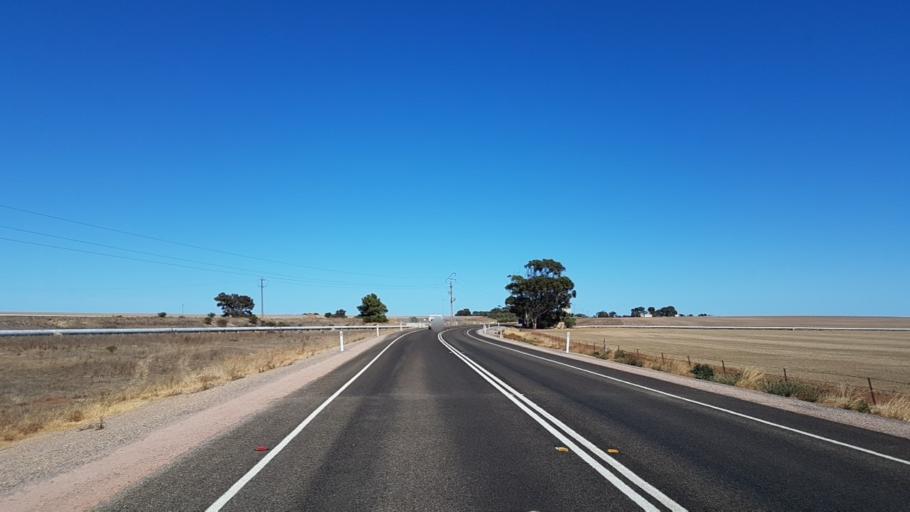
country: AU
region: South Australia
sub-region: Copper Coast
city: Kadina
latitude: -34.0413
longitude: 137.9208
